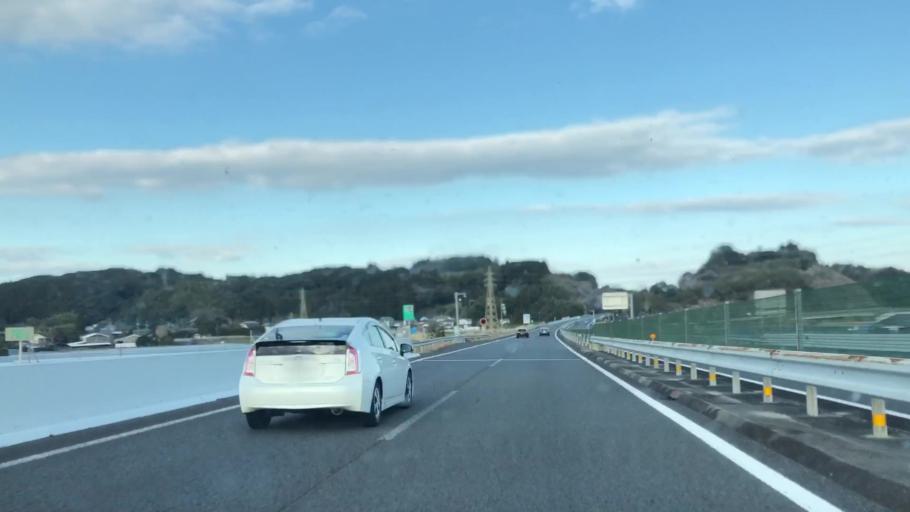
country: JP
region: Miyazaki
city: Miyazaki-shi
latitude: 31.8600
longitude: 131.3786
